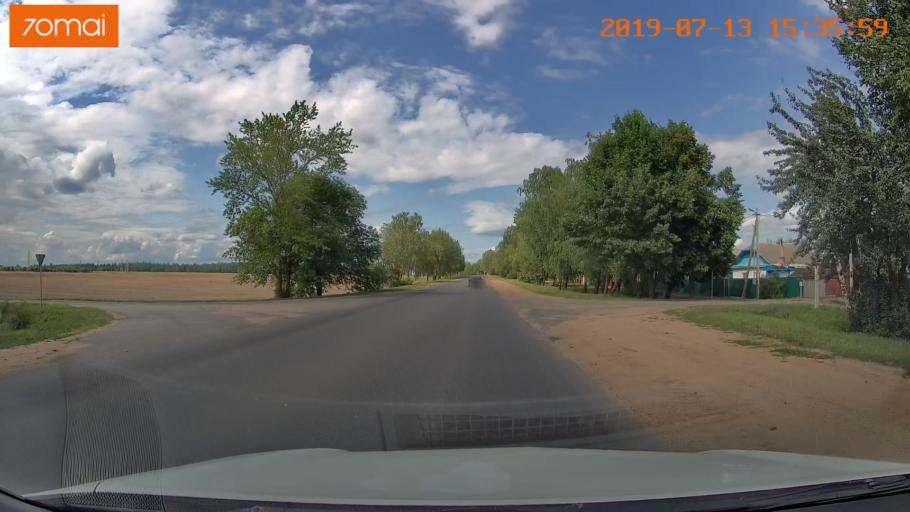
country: BY
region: Mogilev
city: Babruysk
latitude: 53.1274
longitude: 29.1667
